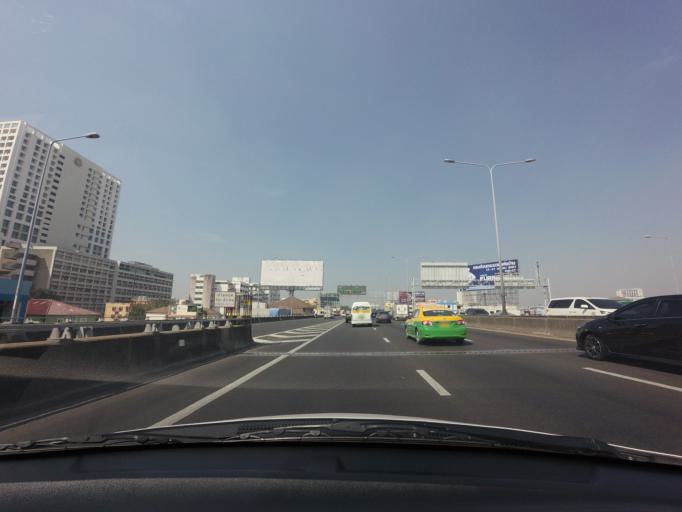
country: TH
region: Bangkok
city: Ratchathewi
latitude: 13.7691
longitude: 100.5366
